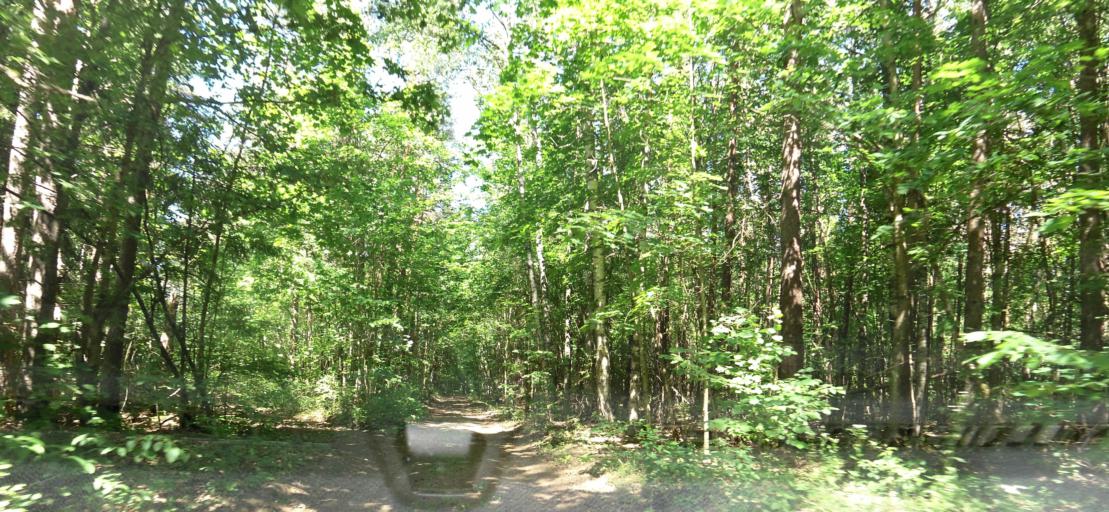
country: LT
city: Grigiskes
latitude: 54.7897
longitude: 24.9657
